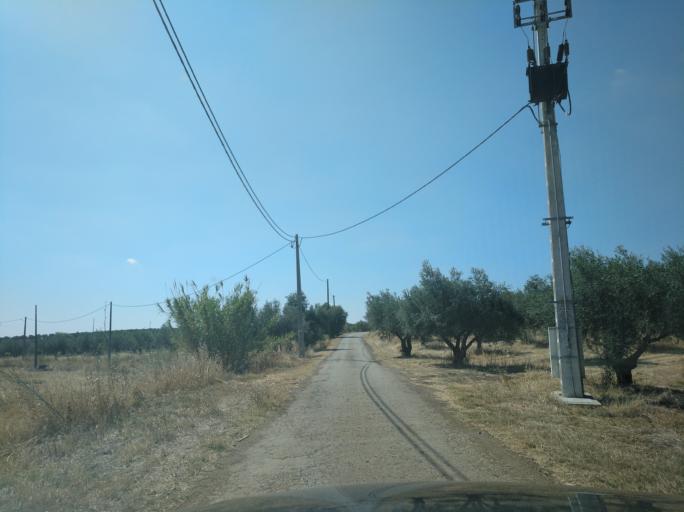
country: PT
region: Portalegre
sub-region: Campo Maior
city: Campo Maior
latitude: 39.0243
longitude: -7.1019
